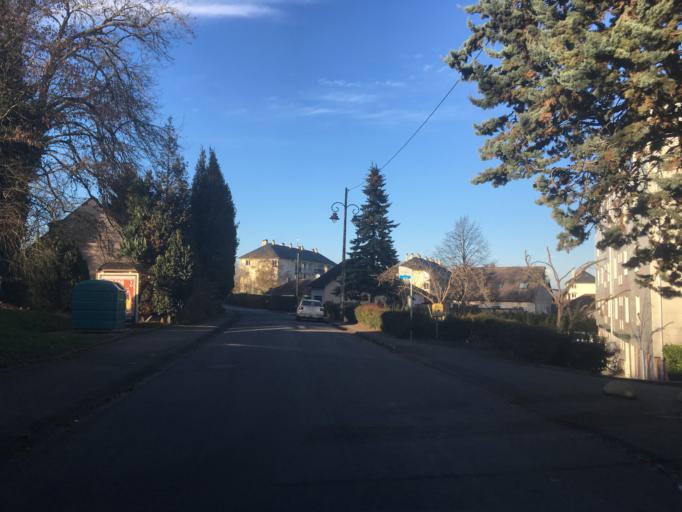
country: FR
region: Haute-Normandie
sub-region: Departement de l'Eure
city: Saint-Marcel
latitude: 49.1019
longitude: 1.4435
